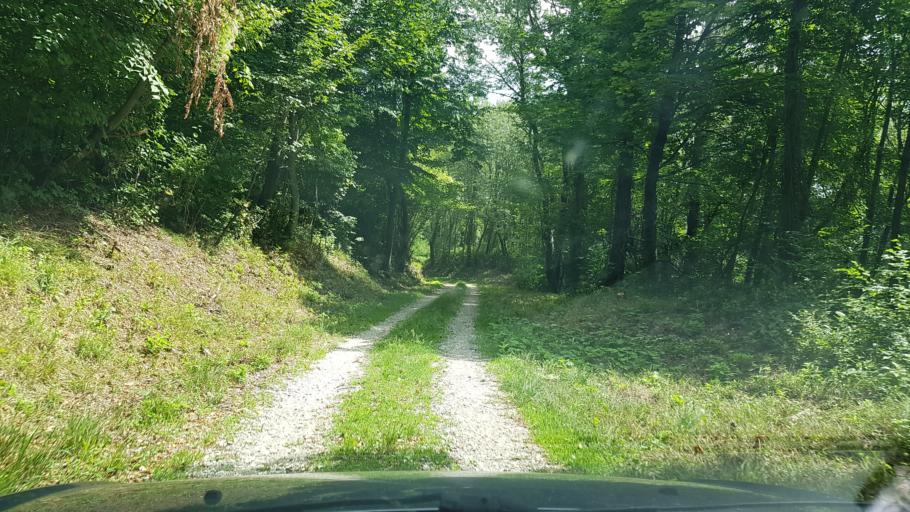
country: SI
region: Nova Gorica
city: Solkan
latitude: 46.0162
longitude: 13.6428
